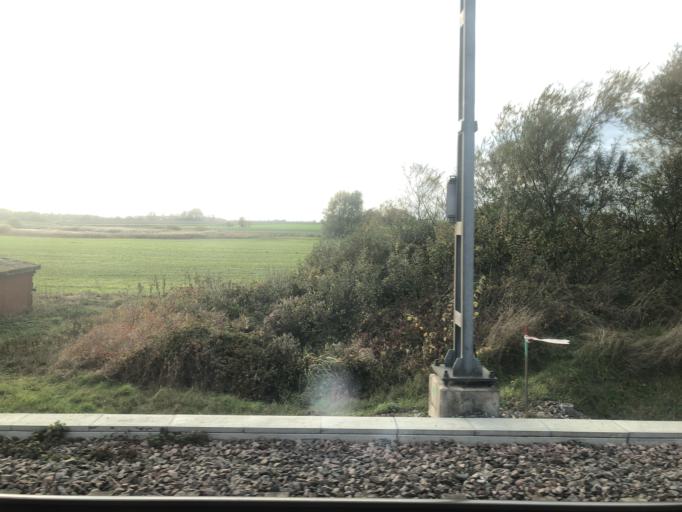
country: SE
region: Skane
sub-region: Lomma Kommun
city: Lomma
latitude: 55.7229
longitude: 13.0748
